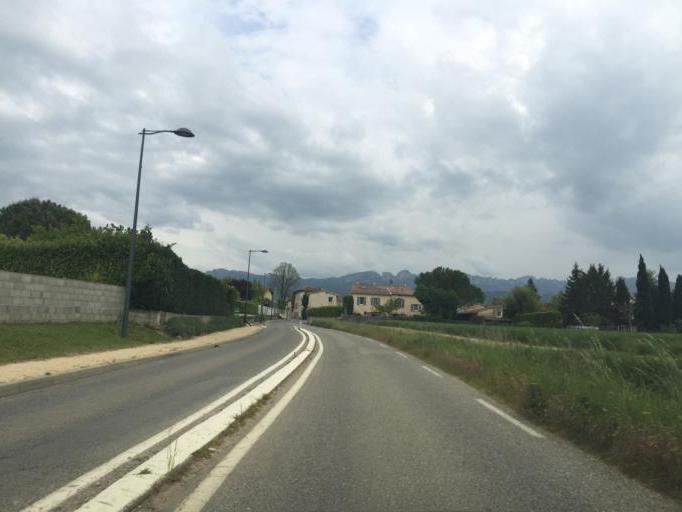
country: FR
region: Rhone-Alpes
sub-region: Departement de la Drome
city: Chatuzange-le-Goubet
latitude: 44.9651
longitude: 5.0739
